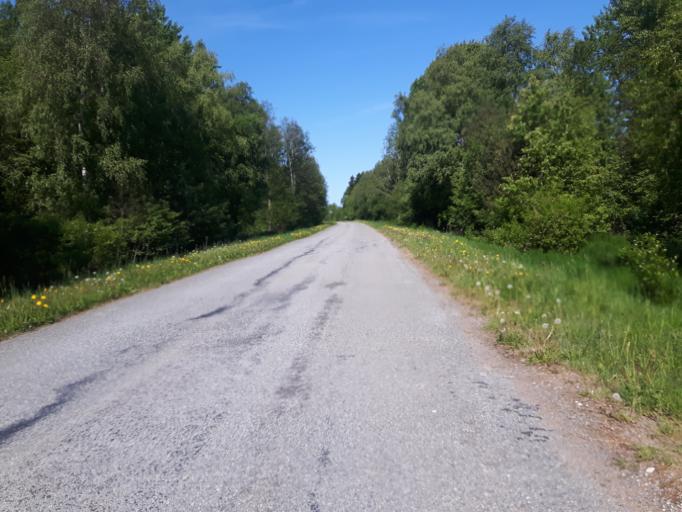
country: EE
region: Ida-Virumaa
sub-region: Aseri vald
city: Aseri
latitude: 59.4520
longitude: 26.8541
